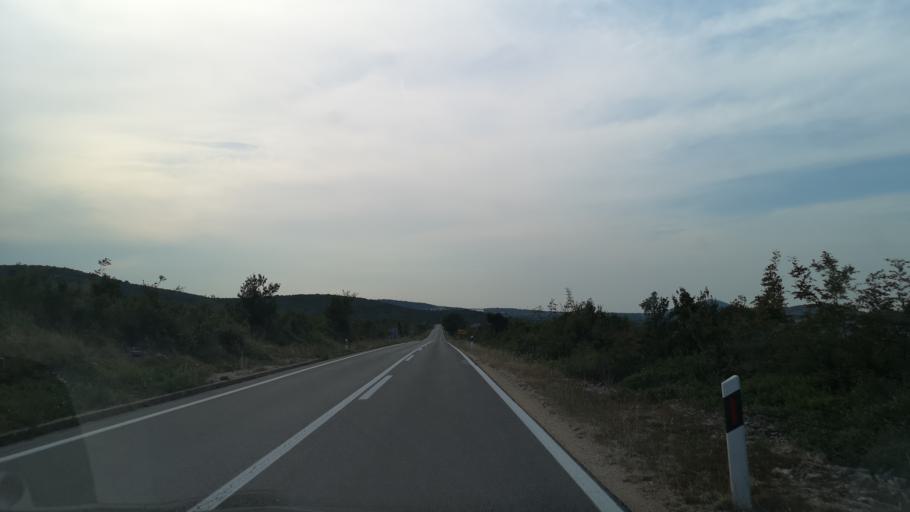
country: HR
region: Sibensko-Kniniska
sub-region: Grad Sibenik
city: Pirovac
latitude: 43.8576
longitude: 15.7549
